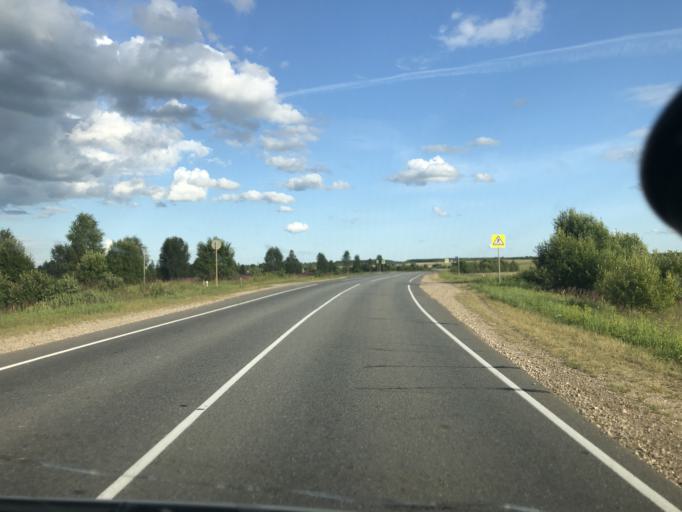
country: RU
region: Kaluga
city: Yukhnov
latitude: 54.7064
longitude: 35.2661
